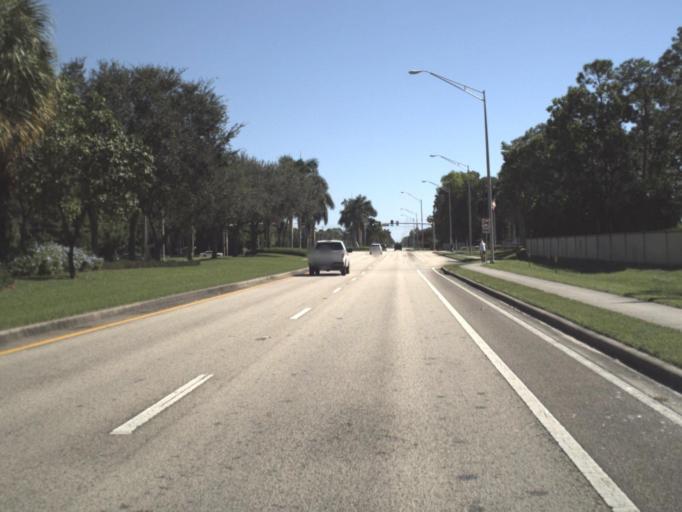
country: US
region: Florida
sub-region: Collier County
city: Lely
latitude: 26.1386
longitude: -81.7471
